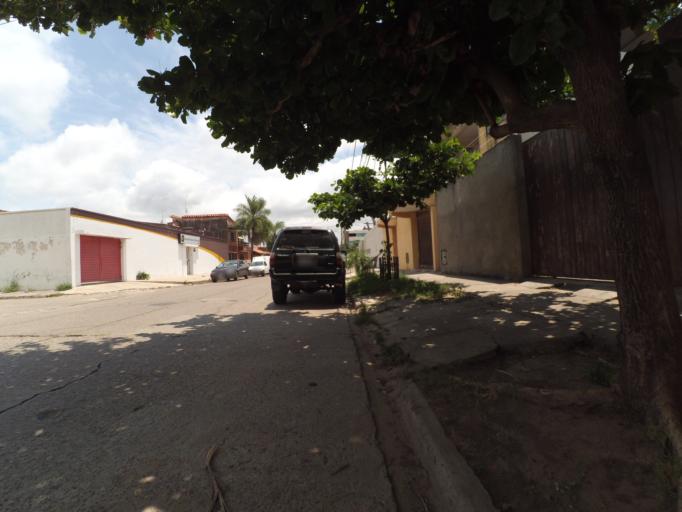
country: BO
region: Santa Cruz
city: Santa Cruz de la Sierra
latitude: -17.7860
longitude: -63.1997
